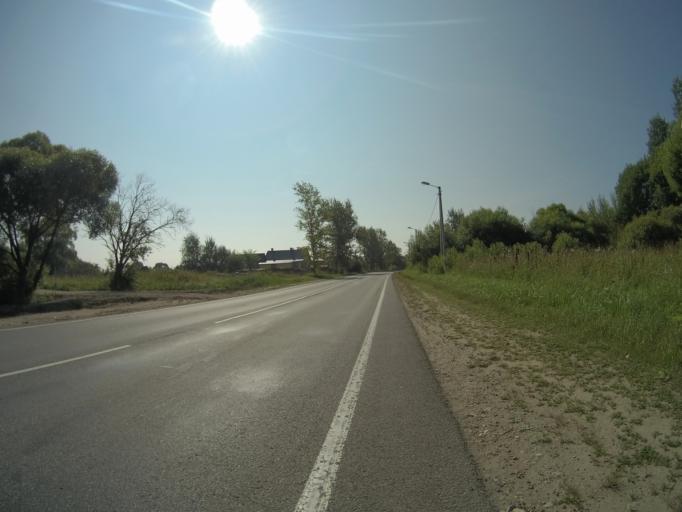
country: RU
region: Vladimir
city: Golovino
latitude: 55.9189
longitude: 40.6060
